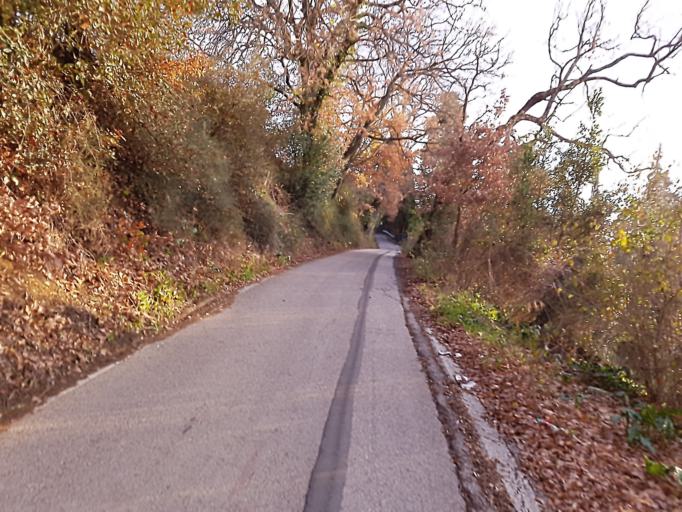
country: IT
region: Umbria
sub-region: Provincia di Perugia
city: Perugia
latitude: 43.0976
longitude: 12.3787
